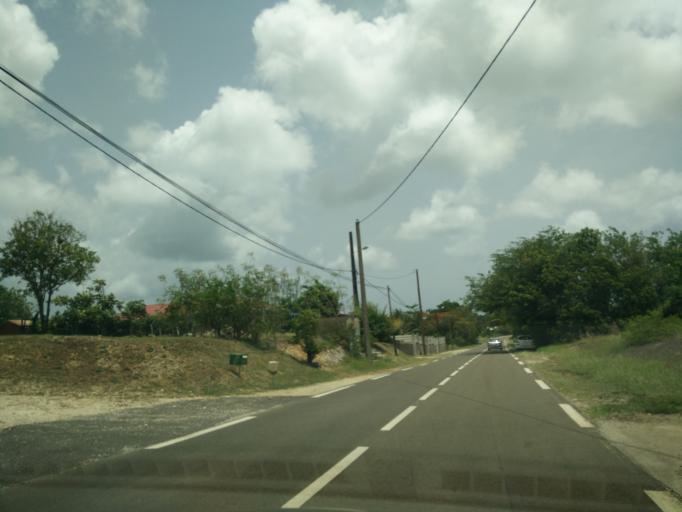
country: GP
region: Guadeloupe
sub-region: Guadeloupe
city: Port-Louis
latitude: 16.4413
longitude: -61.5142
